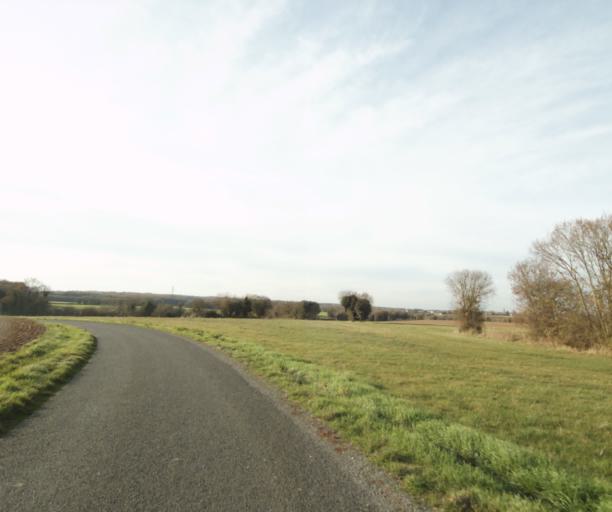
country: FR
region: Poitou-Charentes
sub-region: Departement de la Charente-Maritime
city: Fontcouverte
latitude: 45.8188
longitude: -0.5827
